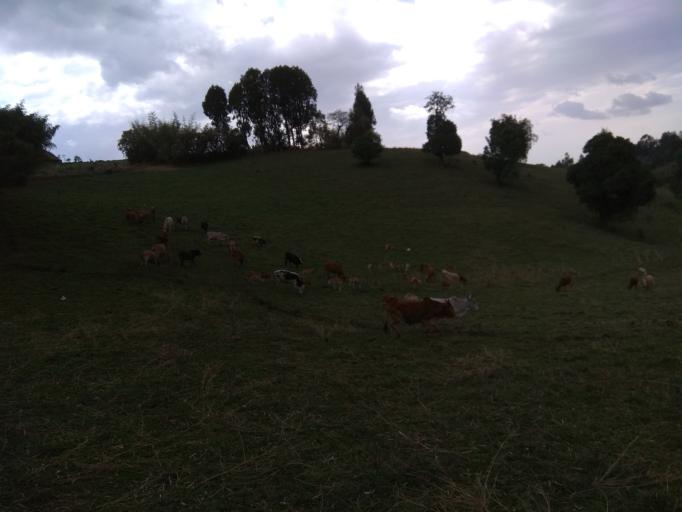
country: ET
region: Oromiya
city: Guder
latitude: 8.7524
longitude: 37.6272
